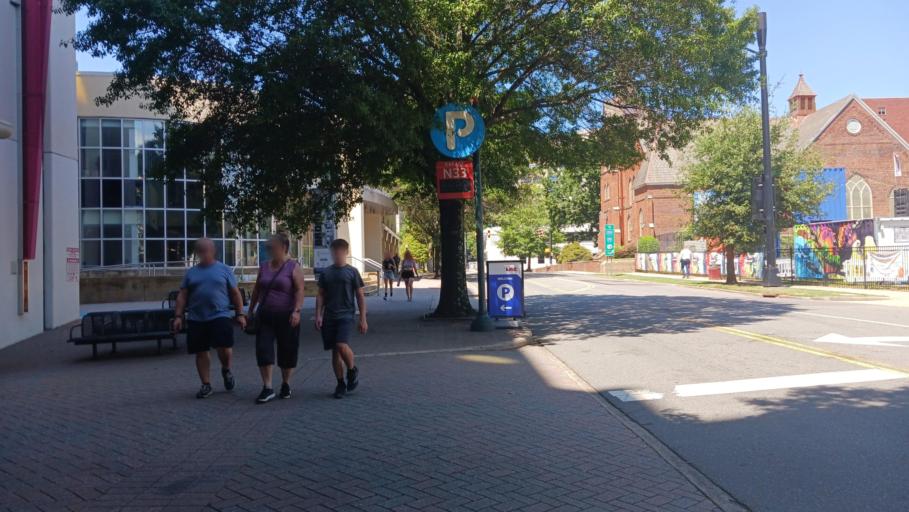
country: US
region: North Carolina
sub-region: Mecklenburg County
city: Charlotte
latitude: 35.2279
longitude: -80.8380
